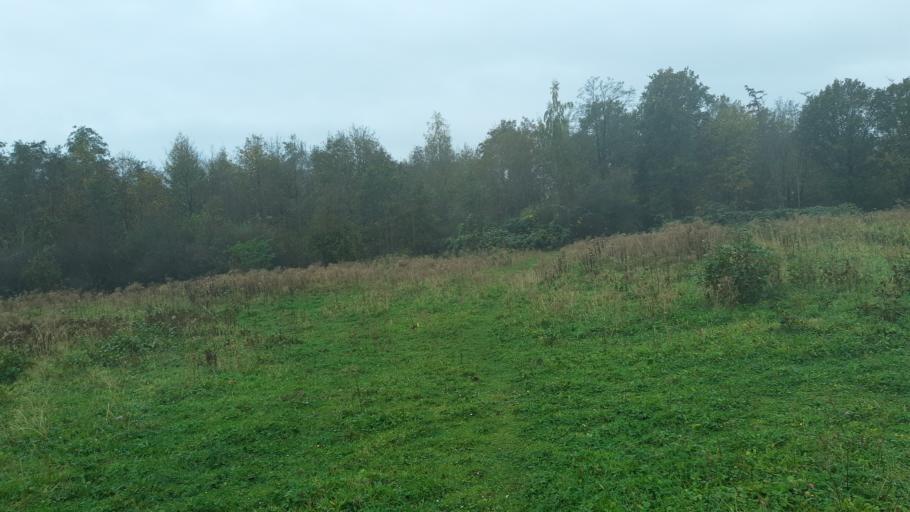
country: NL
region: Friesland
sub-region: Gemeente Lemsterland
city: Echtenerbrug
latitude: 52.7856
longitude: 5.8048
